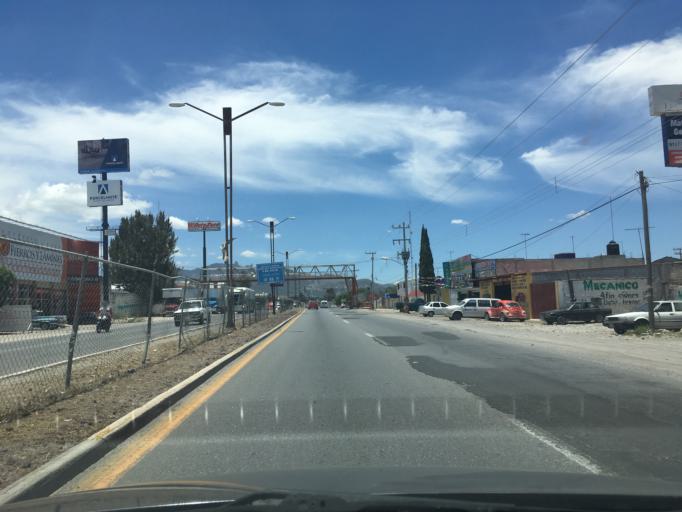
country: MX
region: Hidalgo
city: Actopan
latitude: 20.2779
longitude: -98.9578
